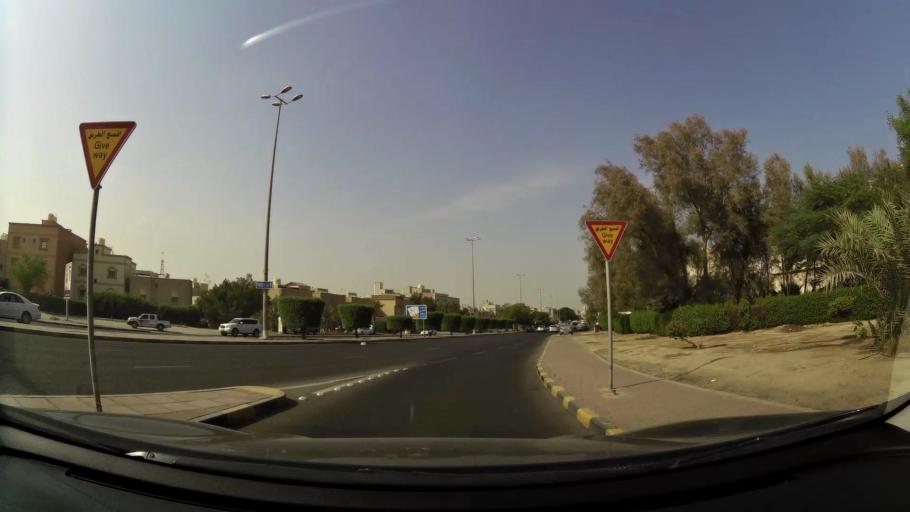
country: KW
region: Al Ahmadi
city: Ar Riqqah
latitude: 29.1573
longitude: 48.0863
